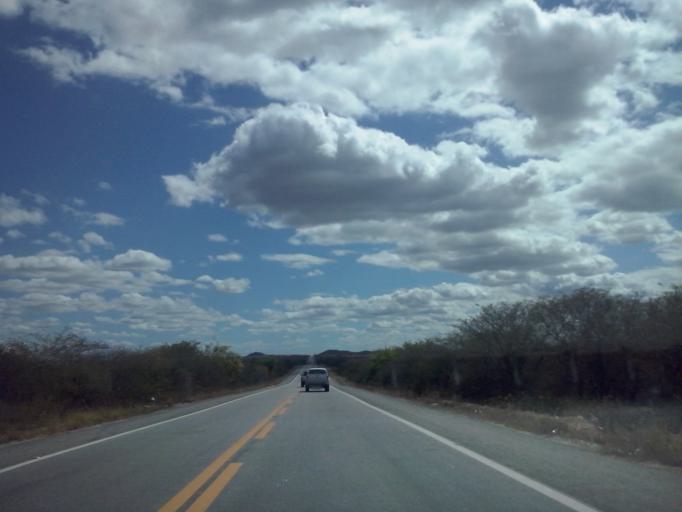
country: BR
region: Paraiba
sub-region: Soledade
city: Soledade
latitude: -7.0382
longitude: -36.4282
